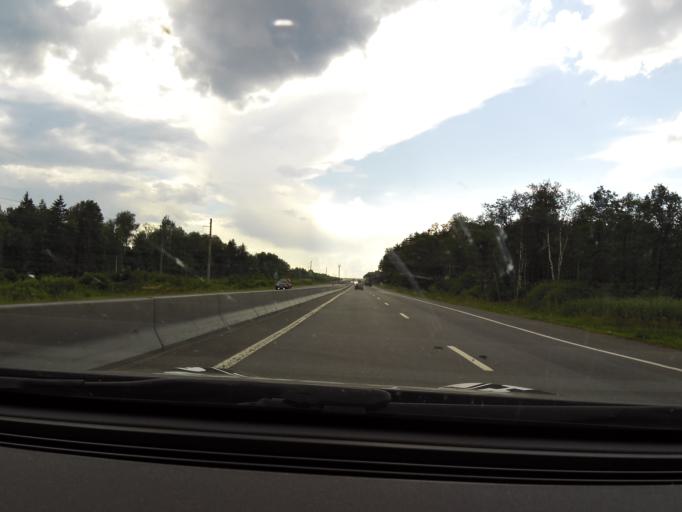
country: RU
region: Nizjnij Novgorod
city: Smolino
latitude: 56.2822
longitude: 43.1035
